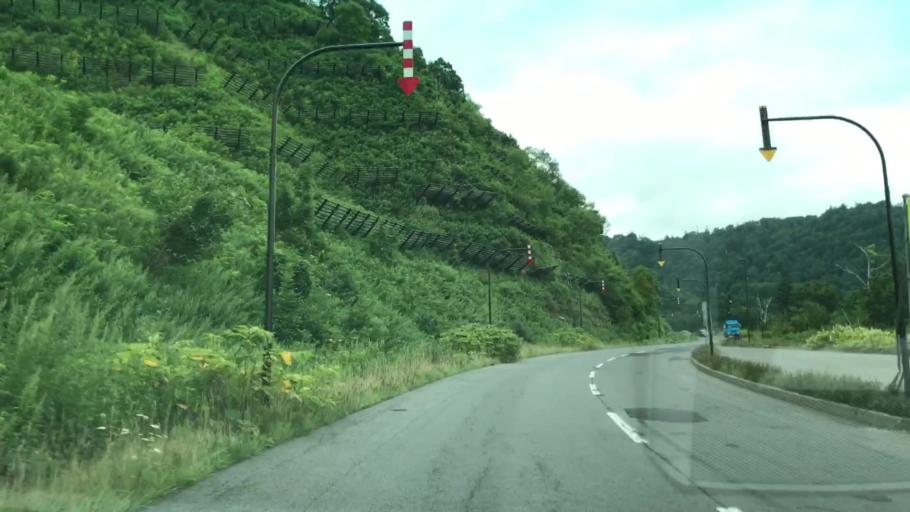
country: JP
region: Hokkaido
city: Otaru
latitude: 42.9908
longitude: 140.8757
